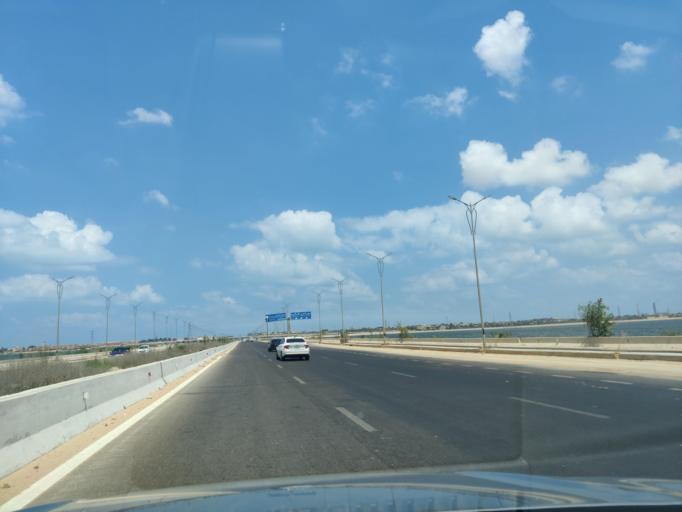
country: EG
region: Alexandria
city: Alexandria
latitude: 30.9927
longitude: 29.6489
